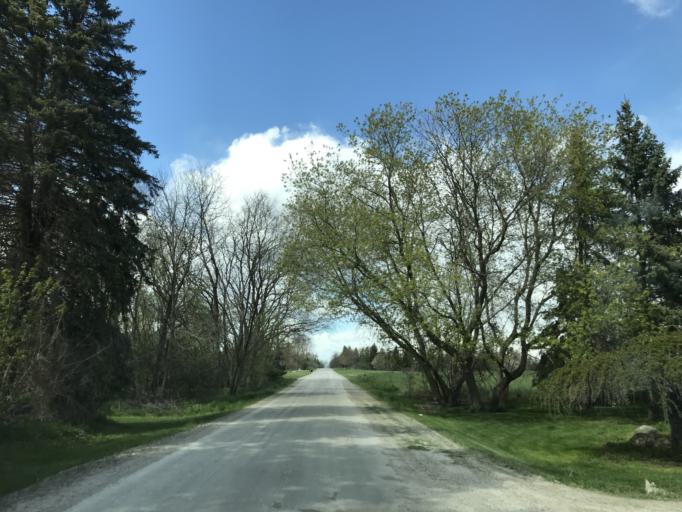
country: US
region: Michigan
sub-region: Oakland County
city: South Lyon
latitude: 42.3901
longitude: -83.6634
